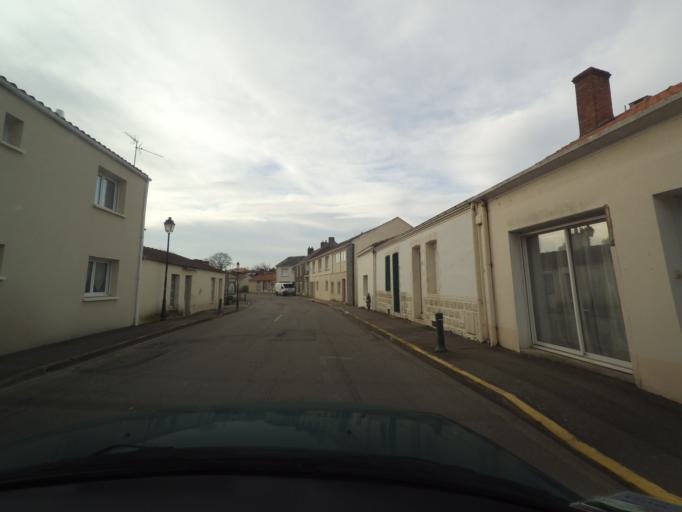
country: FR
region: Pays de la Loire
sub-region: Departement de la Loire-Atlantique
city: Saint-Pere-en-Retz
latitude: 47.2067
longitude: -2.0467
